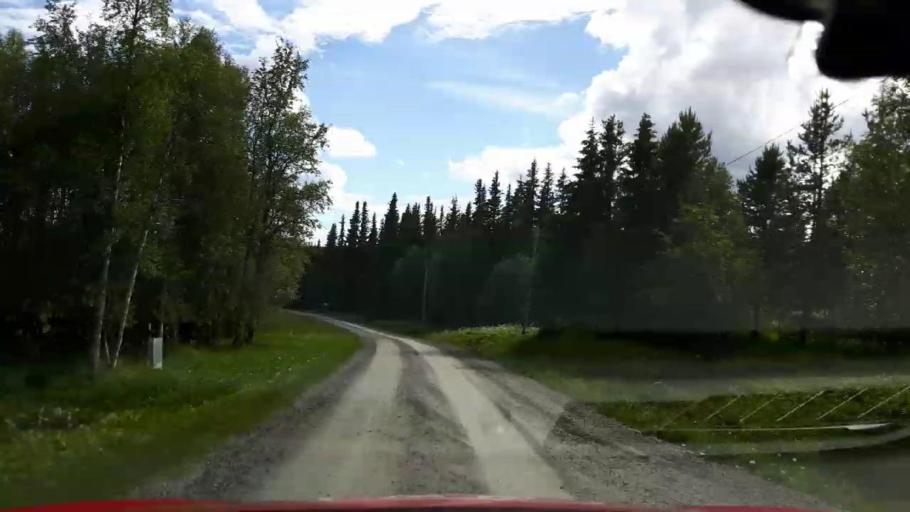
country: SE
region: Jaemtland
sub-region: Krokoms Kommun
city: Valla
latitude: 63.8361
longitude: 14.0417
